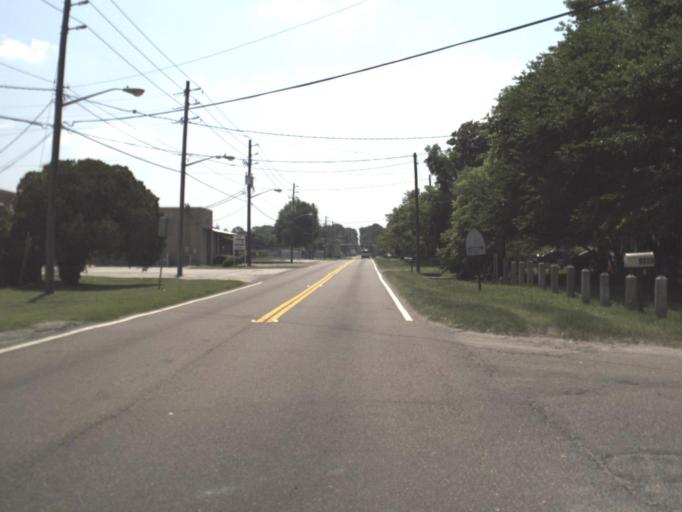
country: US
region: Florida
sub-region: Duval County
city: Jacksonville
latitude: 30.3637
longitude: -81.7360
